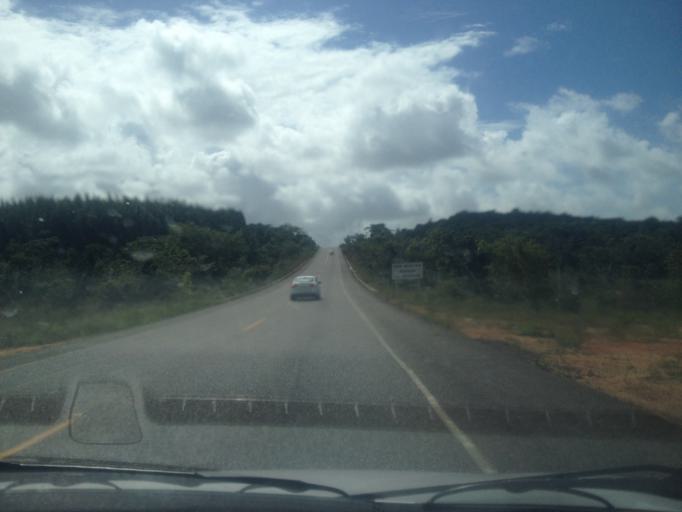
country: BR
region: Bahia
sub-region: Entre Rios
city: Entre Rios
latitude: -12.2261
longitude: -37.8375
